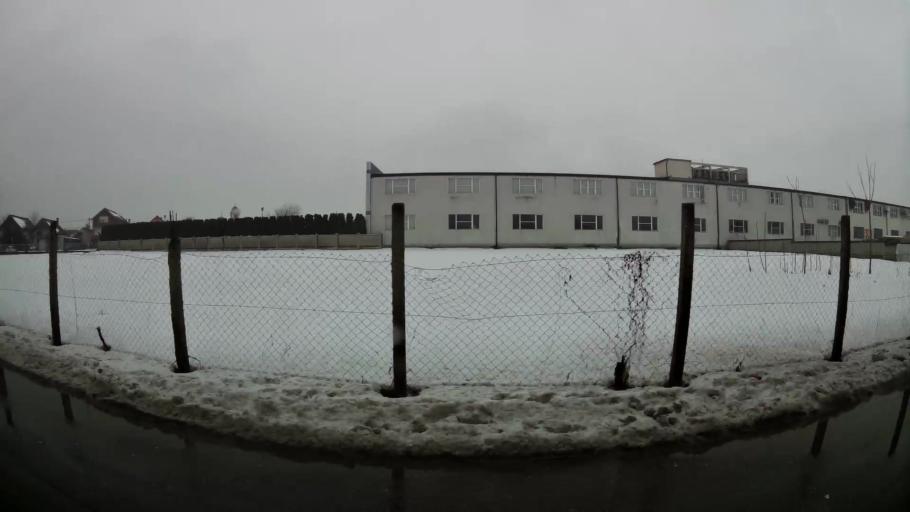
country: RS
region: Central Serbia
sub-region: Belgrade
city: Zemun
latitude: 44.8470
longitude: 20.3610
